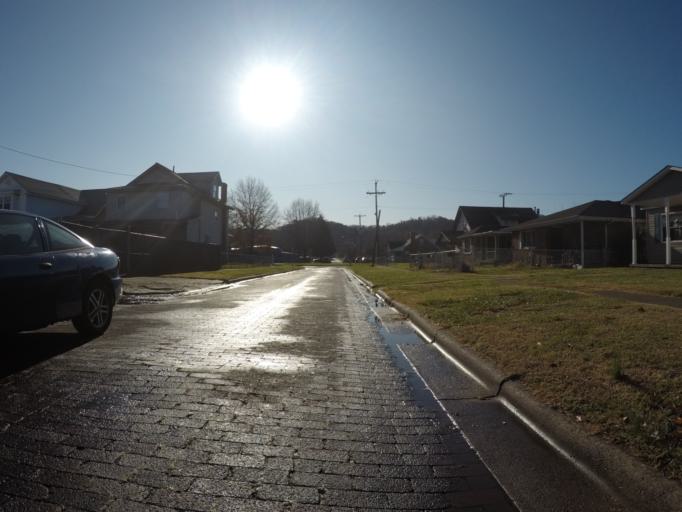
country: US
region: Ohio
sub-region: Lawrence County
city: Burlington
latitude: 38.4049
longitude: -82.5072
